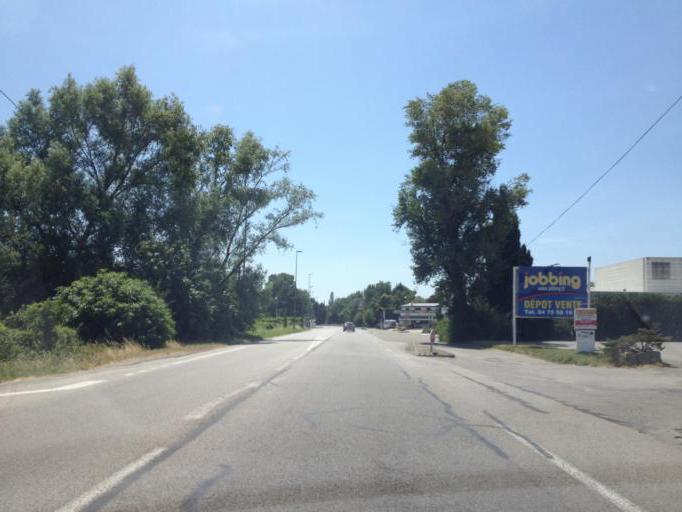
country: FR
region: Rhone-Alpes
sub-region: Departement de l'Ardeche
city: Guilherand-Granges
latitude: 44.9211
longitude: 4.8791
